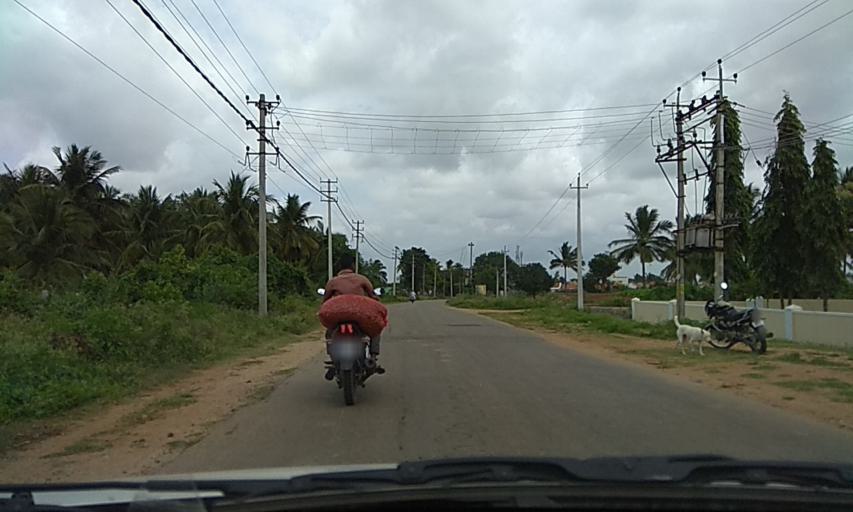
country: IN
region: Karnataka
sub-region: Chamrajnagar
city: Gundlupet
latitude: 11.8079
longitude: 76.7923
